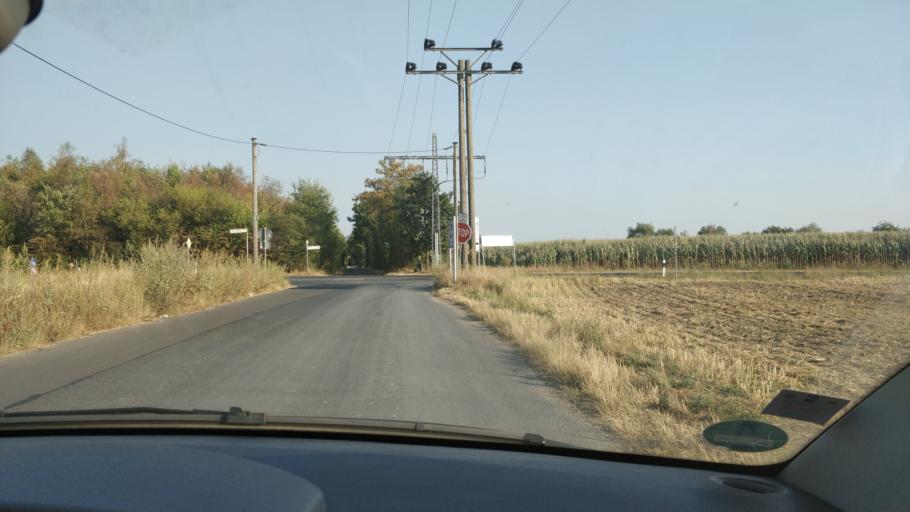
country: DE
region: North Rhine-Westphalia
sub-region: Regierungsbezirk Dusseldorf
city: Dormagen
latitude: 51.0959
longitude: 6.7758
